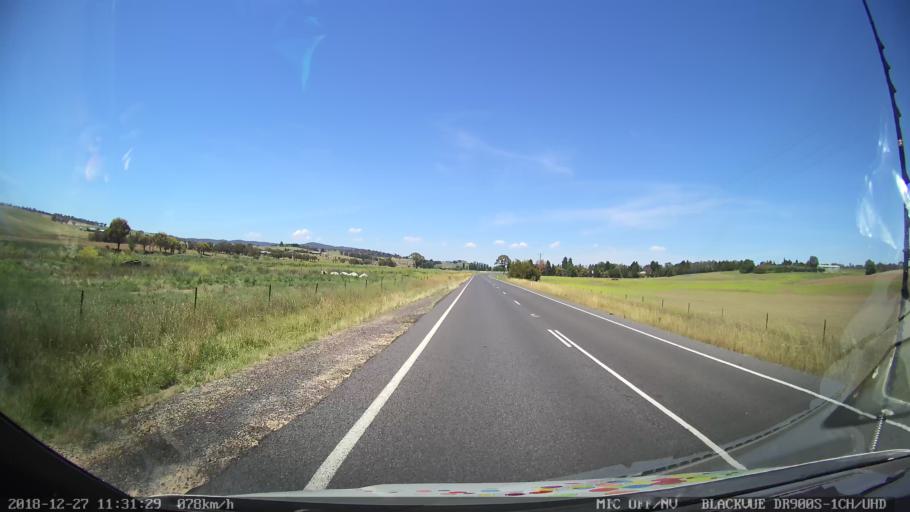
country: AU
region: New South Wales
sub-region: Bathurst Regional
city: Perthville
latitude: -33.4959
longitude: 149.5391
